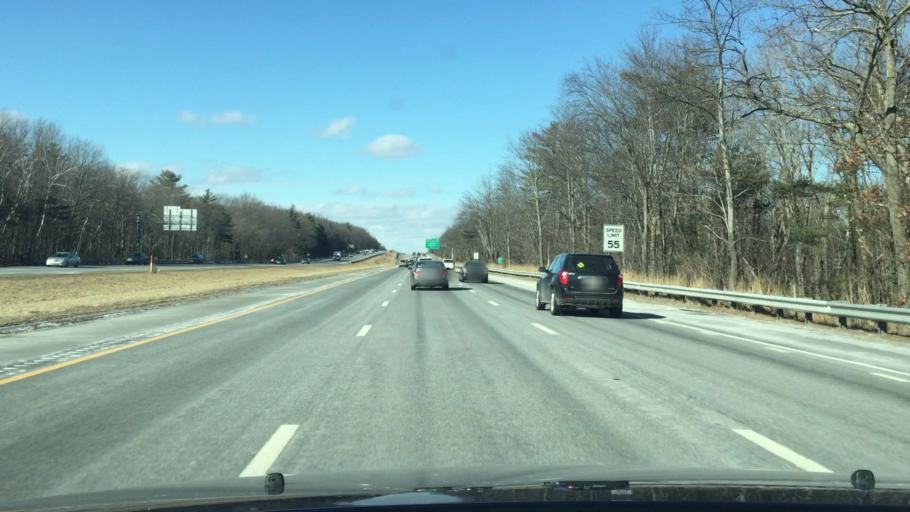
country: US
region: Massachusetts
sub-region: Middlesex County
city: Tyngsboro
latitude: 42.6385
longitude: -71.4113
